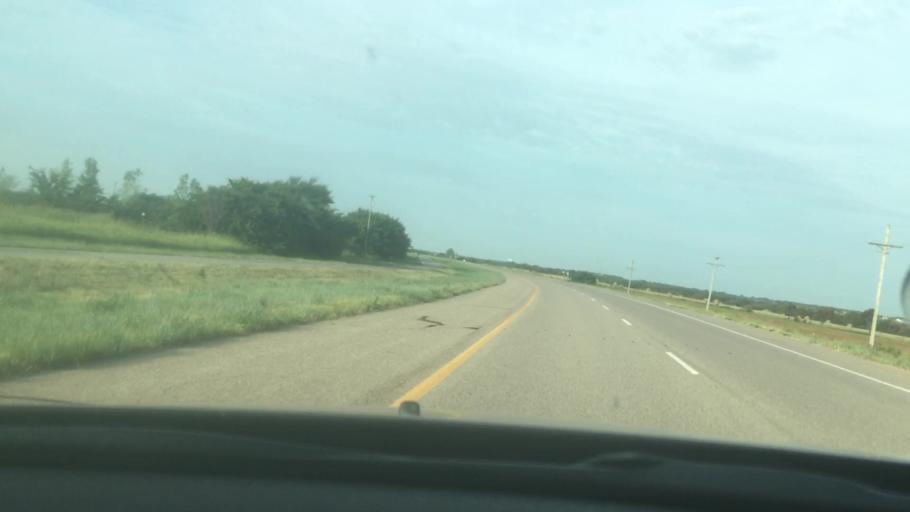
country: US
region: Oklahoma
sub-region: Pontotoc County
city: Ada
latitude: 34.7158
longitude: -96.7248
